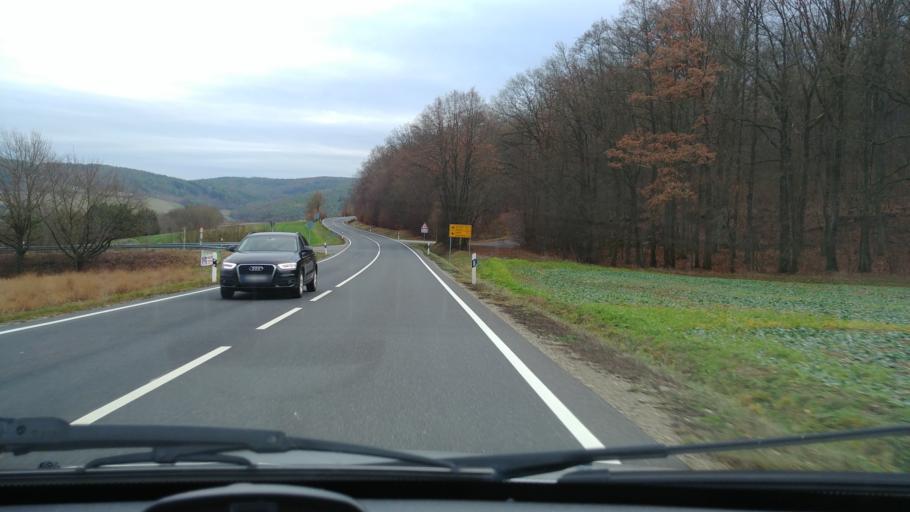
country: DE
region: Bavaria
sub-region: Regierungsbezirk Unterfranken
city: Eussenheim
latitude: 49.9589
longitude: 9.8042
